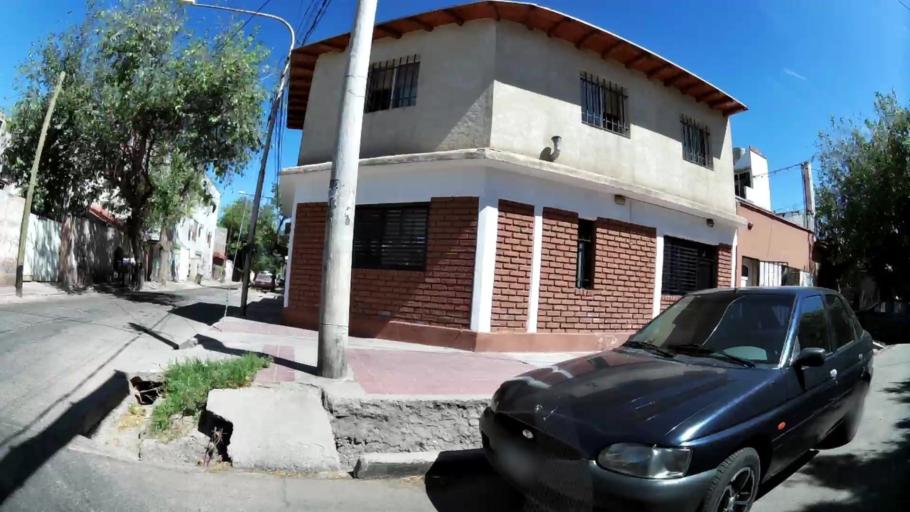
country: AR
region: Mendoza
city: Las Heras
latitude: -32.8527
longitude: -68.8350
